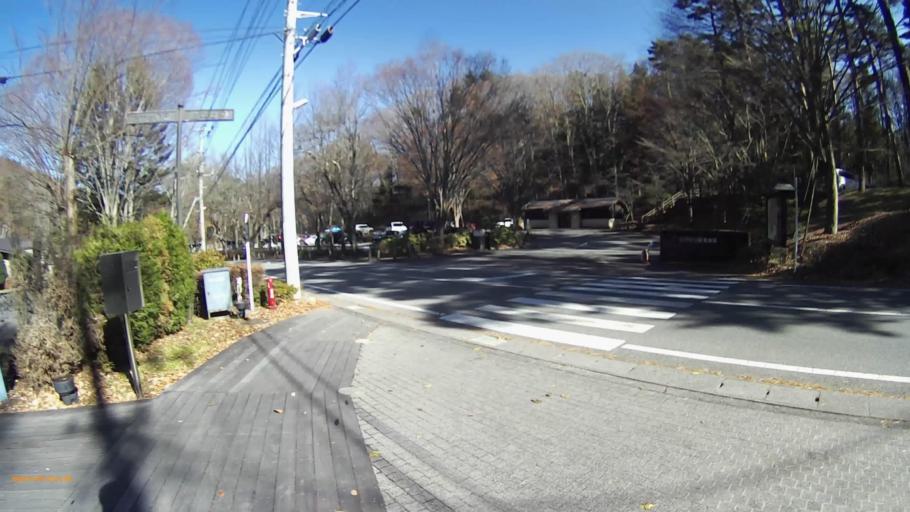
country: JP
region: Yamanashi
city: Fujikawaguchiko
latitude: 35.4555
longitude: 138.8245
